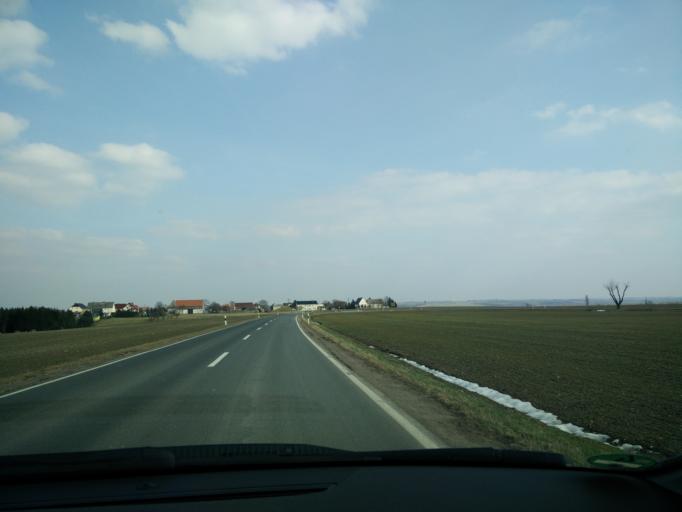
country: DE
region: Saxony
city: Konigsfeld
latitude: 51.0991
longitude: 12.7510
